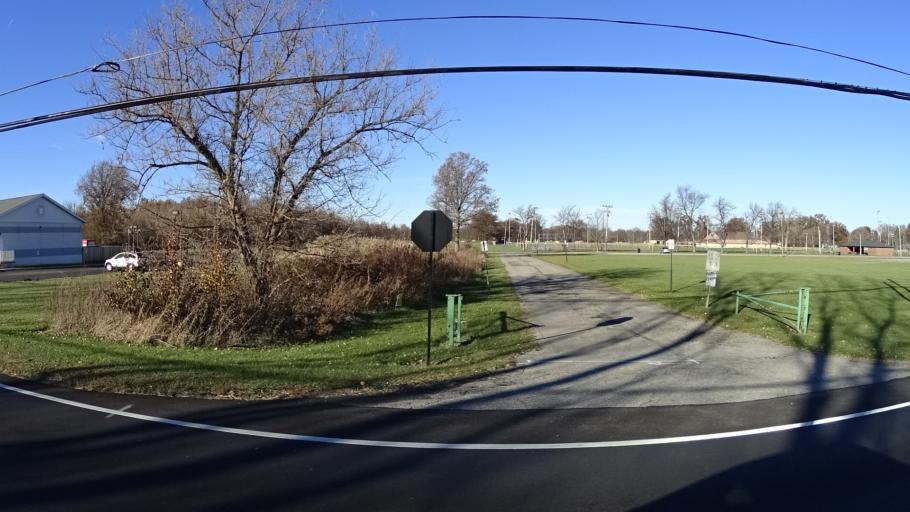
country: US
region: Ohio
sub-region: Lorain County
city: Elyria
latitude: 41.3752
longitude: -82.1362
